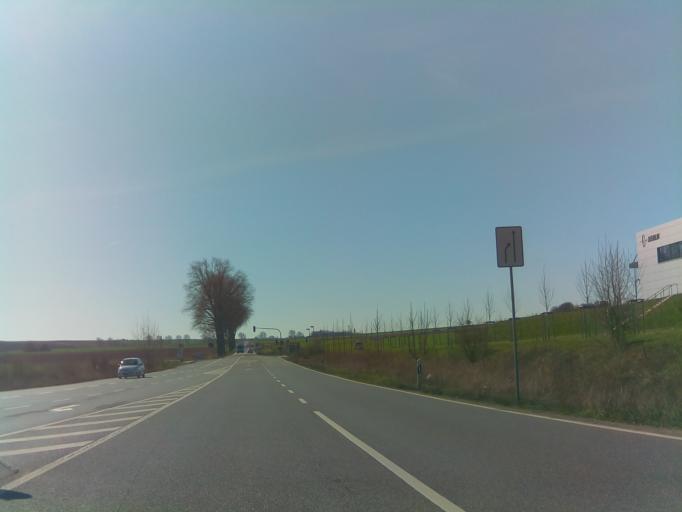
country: DE
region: Rheinland-Pfalz
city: Gau-Bischofsheim
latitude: 49.9457
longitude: 8.2624
